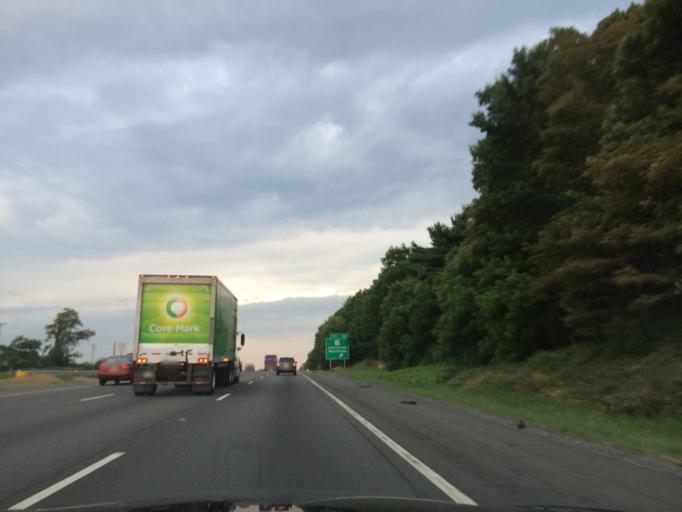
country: US
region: Maryland
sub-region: Frederick County
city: Linganore
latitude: 39.3799
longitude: -77.2509
